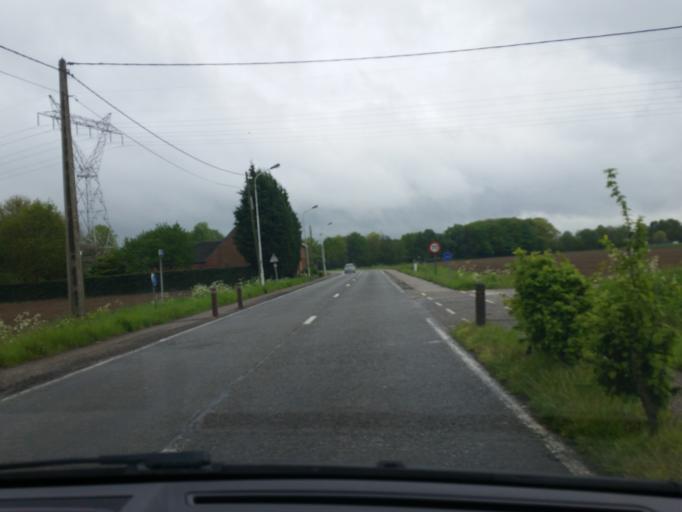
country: BE
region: Flanders
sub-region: Provincie Antwerpen
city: Boechout
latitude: 51.1759
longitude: 4.4881
